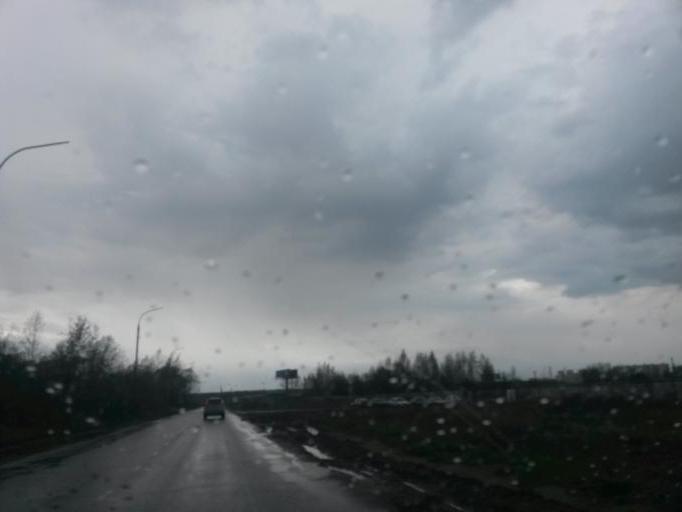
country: RU
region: Moskovskaya
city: Shcherbinka
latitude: 55.5201
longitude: 37.5820
